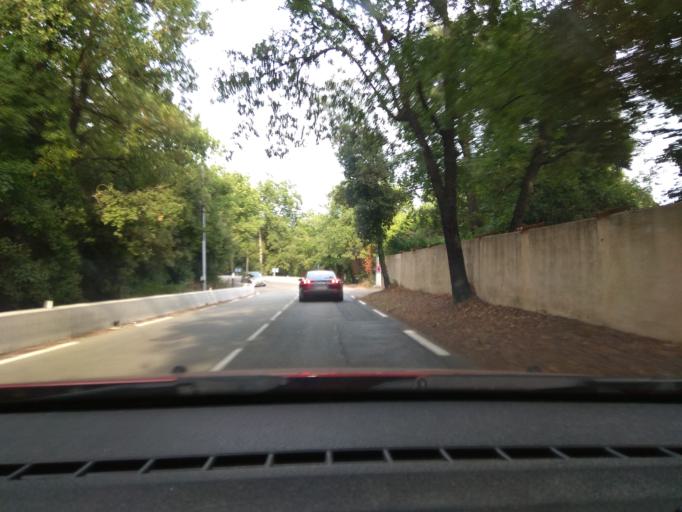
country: FR
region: Provence-Alpes-Cote d'Azur
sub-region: Departement des Alpes-Maritimes
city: Le Rouret
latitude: 43.6508
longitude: 7.0262
